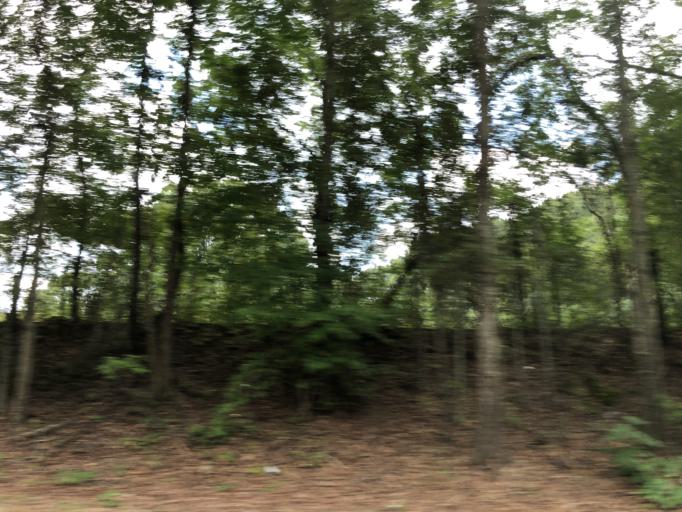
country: US
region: Georgia
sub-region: Barrow County
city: Russell
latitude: 33.9540
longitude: -83.6714
